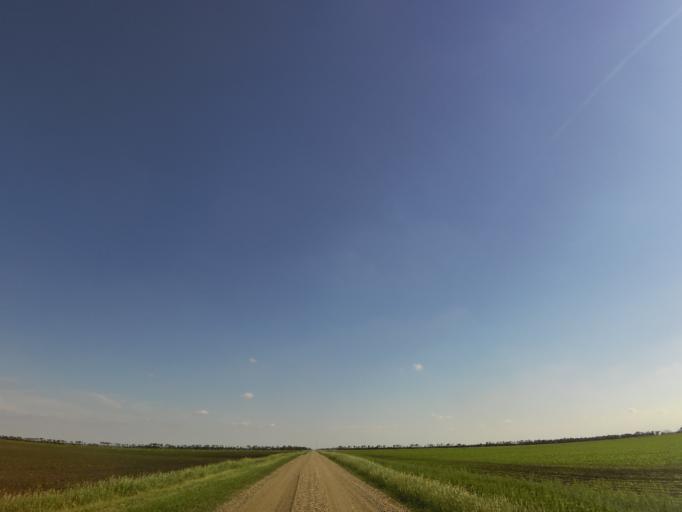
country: US
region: North Dakota
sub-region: Walsh County
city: Grafton
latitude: 48.3425
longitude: -97.2329
